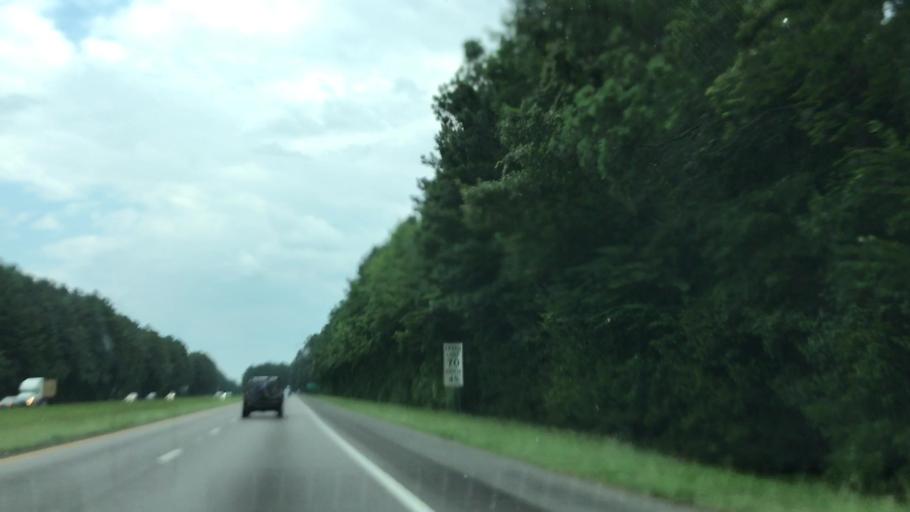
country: US
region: South Carolina
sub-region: Richland County
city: Blythewood
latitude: 34.2692
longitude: -80.9980
